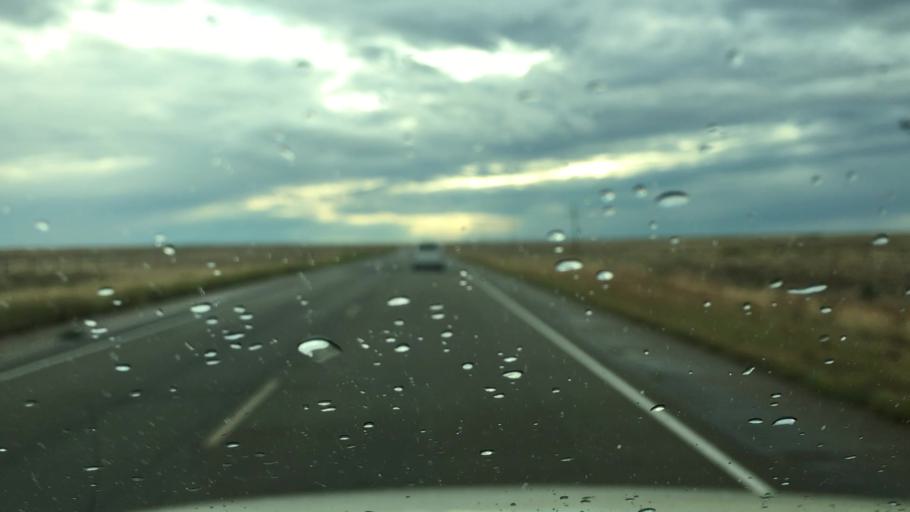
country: US
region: New Mexico
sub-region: Chaves County
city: Roswell
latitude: 33.4049
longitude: -104.3125
